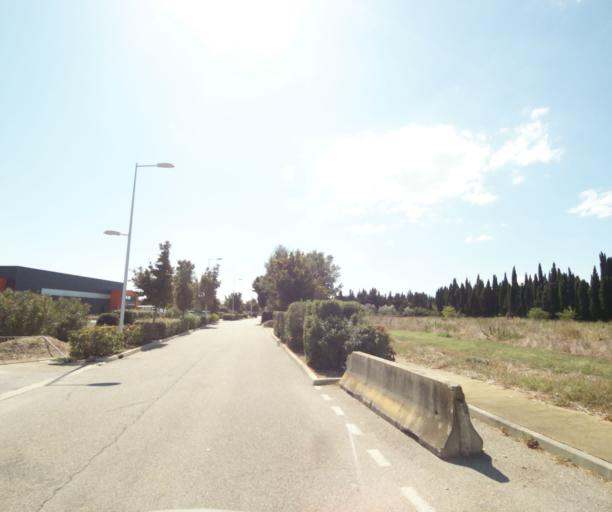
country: FR
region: Languedoc-Roussillon
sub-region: Departement du Gard
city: Bouillargues
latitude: 43.8093
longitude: 4.4113
